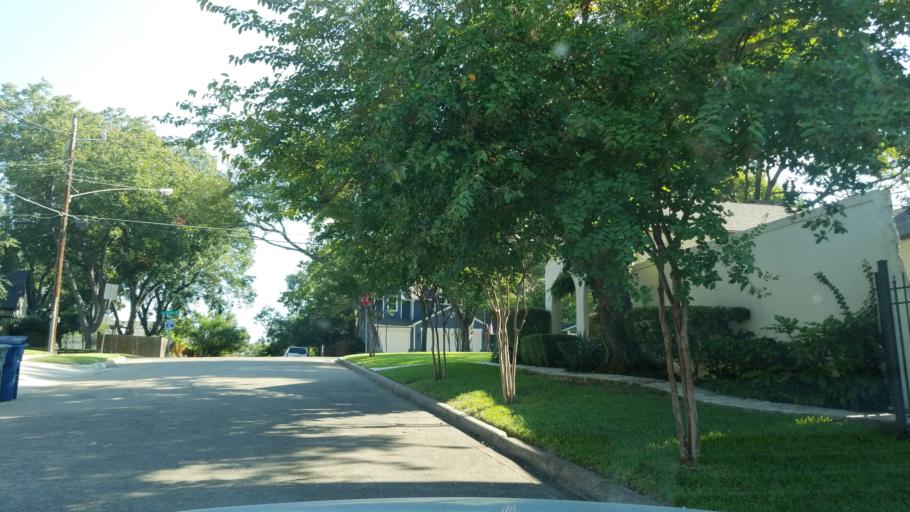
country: US
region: Texas
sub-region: Dallas County
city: Highland Park
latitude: 32.8089
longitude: -96.7344
